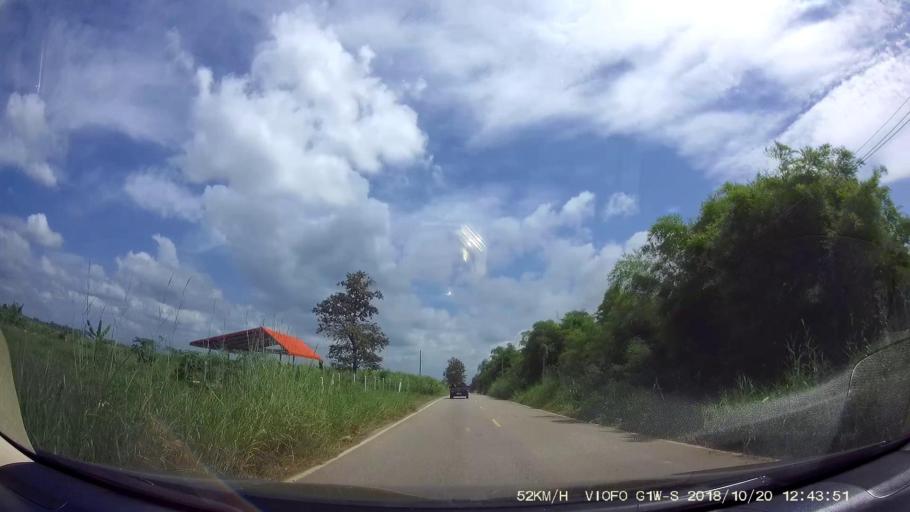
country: TH
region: Chaiyaphum
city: Khon San
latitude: 16.5408
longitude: 101.8642
